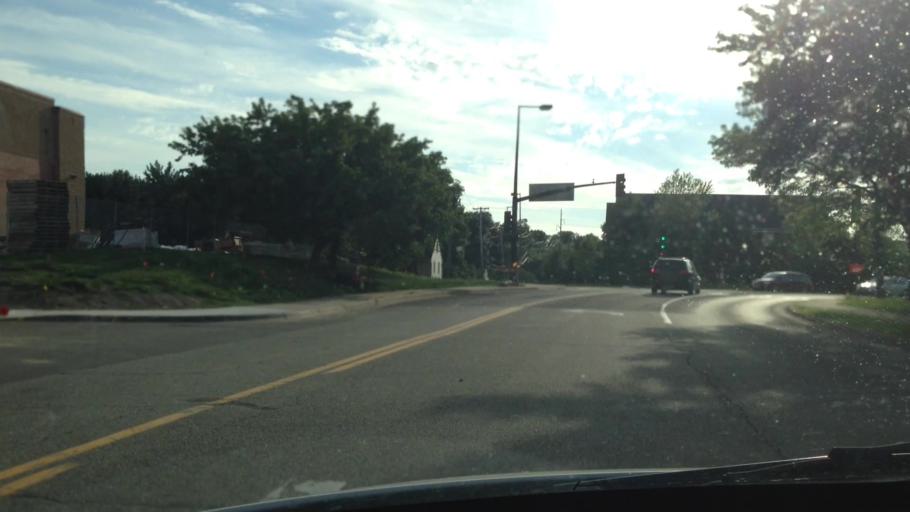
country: US
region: Minnesota
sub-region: Hennepin County
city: Saint Louis Park
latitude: 44.9676
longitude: -93.3541
